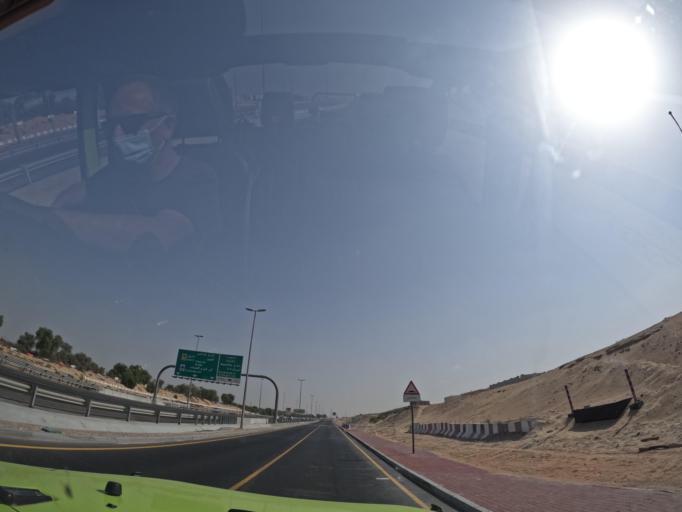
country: AE
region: Ash Shariqah
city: Sharjah
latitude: 25.2062
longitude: 55.4302
